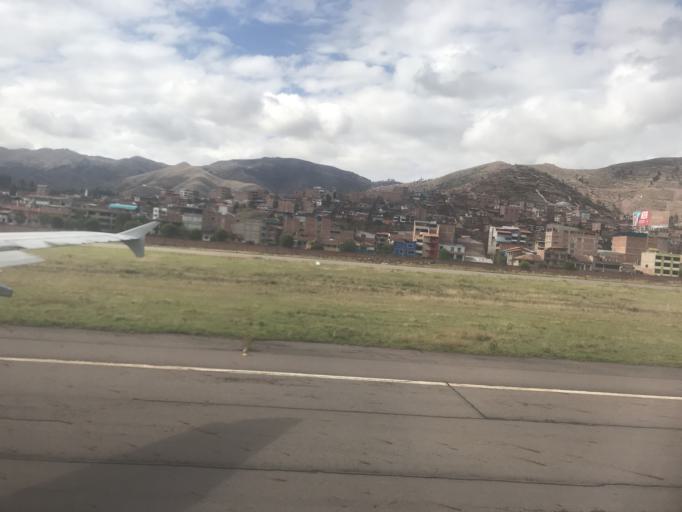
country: PE
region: Cusco
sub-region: Provincia de Cusco
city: Cusco
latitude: -13.5345
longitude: -71.9518
